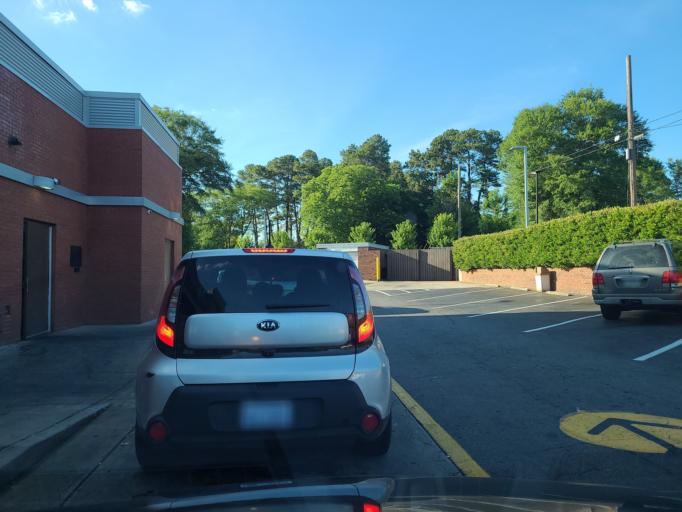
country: US
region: North Carolina
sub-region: Gaston County
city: Ranlo
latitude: 35.2629
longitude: -81.1534
